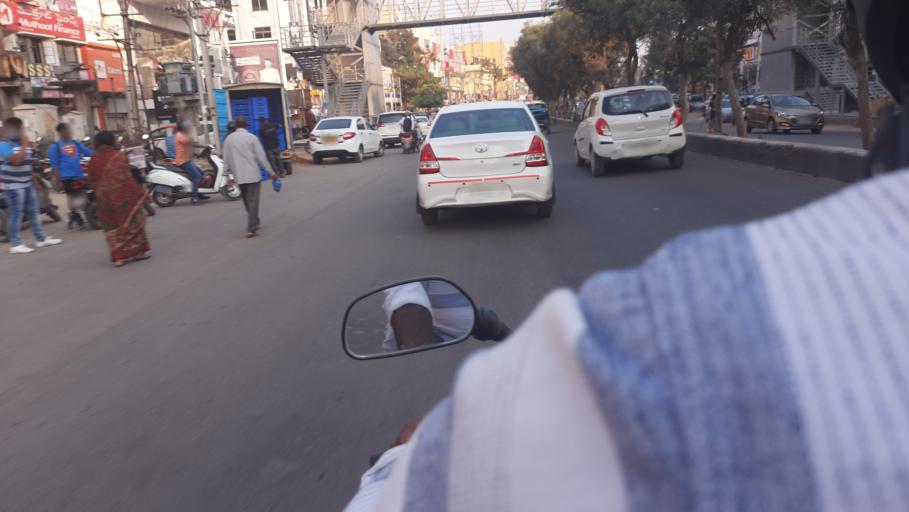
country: IN
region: Telangana
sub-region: Rangareddi
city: Secunderabad
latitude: 17.4814
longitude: 78.5550
